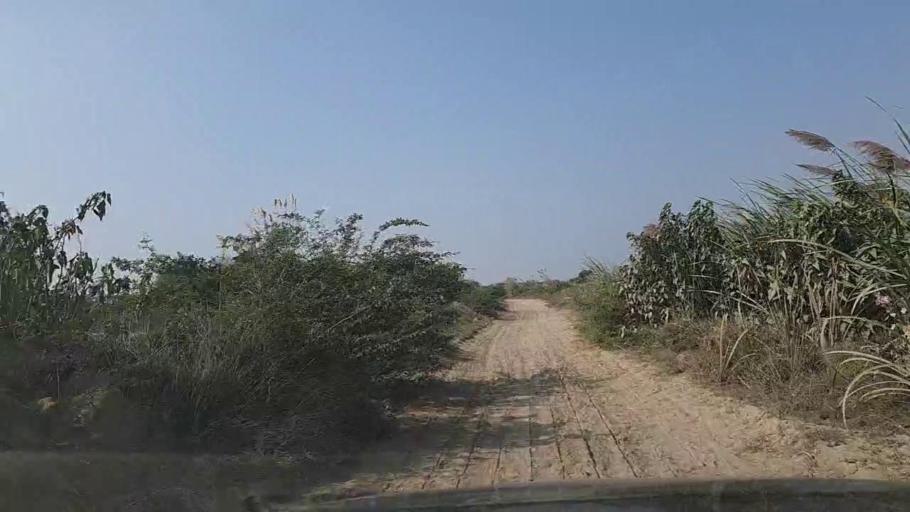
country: PK
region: Sindh
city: Gharo
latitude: 24.7282
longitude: 67.7098
